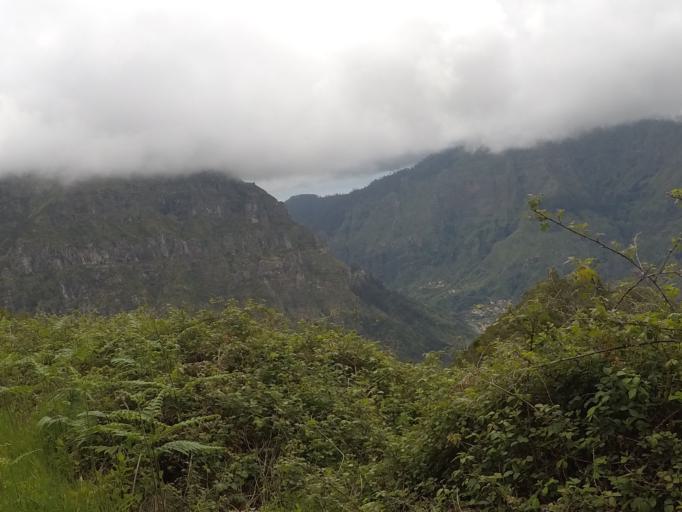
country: PT
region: Madeira
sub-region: Camara de Lobos
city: Curral das Freiras
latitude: 32.7336
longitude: -17.0001
